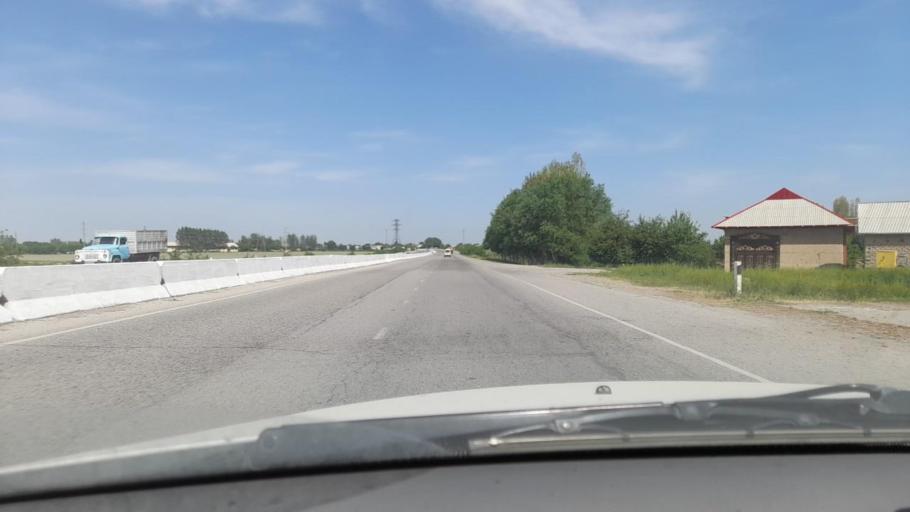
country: UZ
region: Samarqand
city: Kattaqo'rg'on
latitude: 39.9206
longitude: 66.3458
